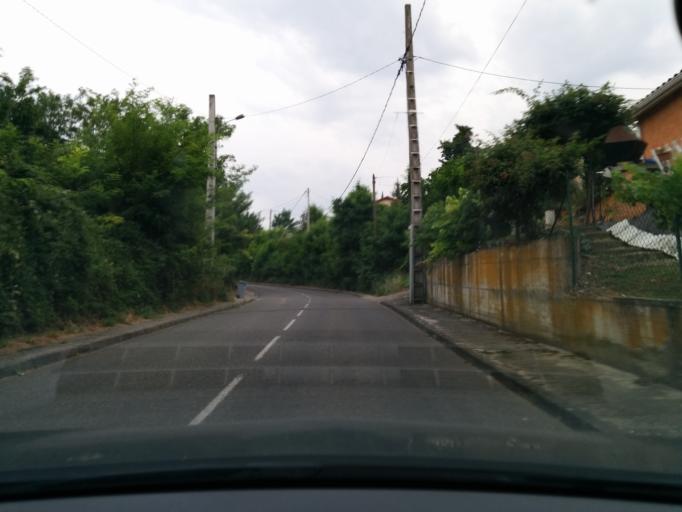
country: FR
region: Midi-Pyrenees
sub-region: Departement de la Haute-Garonne
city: Castanet-Tolosan
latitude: 43.5145
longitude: 1.4909
